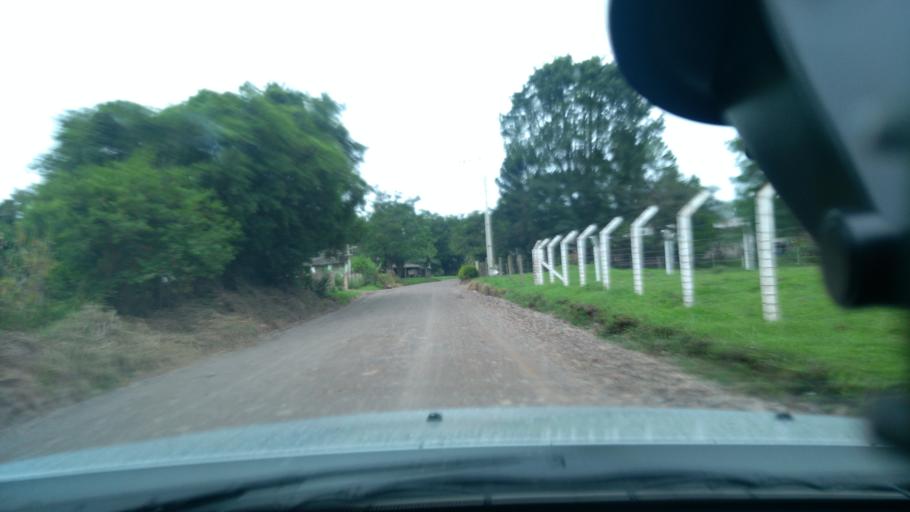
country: BR
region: Rio Grande do Sul
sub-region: Torres
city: Torres
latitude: -29.2099
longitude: -49.9790
